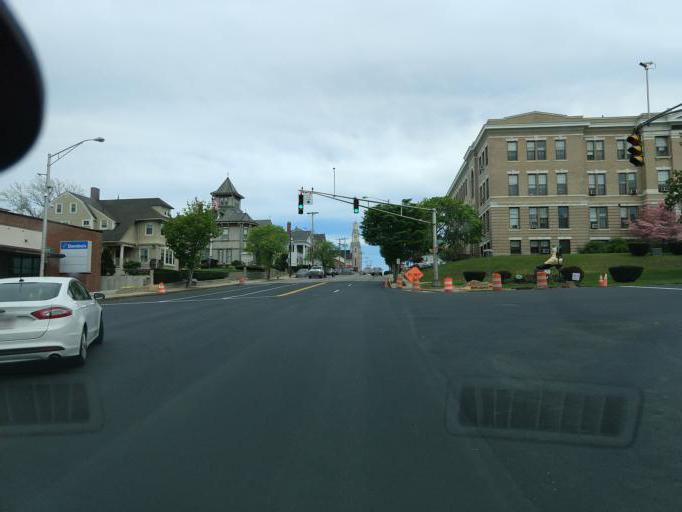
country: US
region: Massachusetts
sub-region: Essex County
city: Haverhill
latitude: 42.7773
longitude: -71.0772
